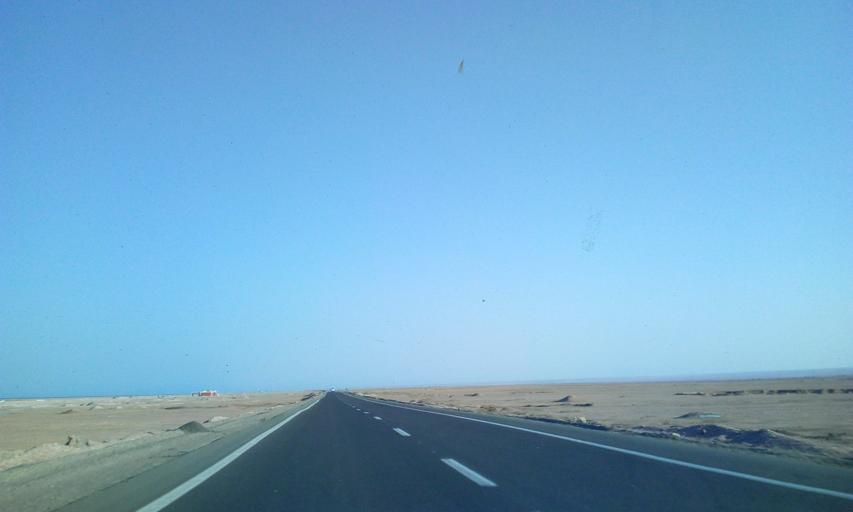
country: EG
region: South Sinai
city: Tor
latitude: 28.6609
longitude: 32.8413
